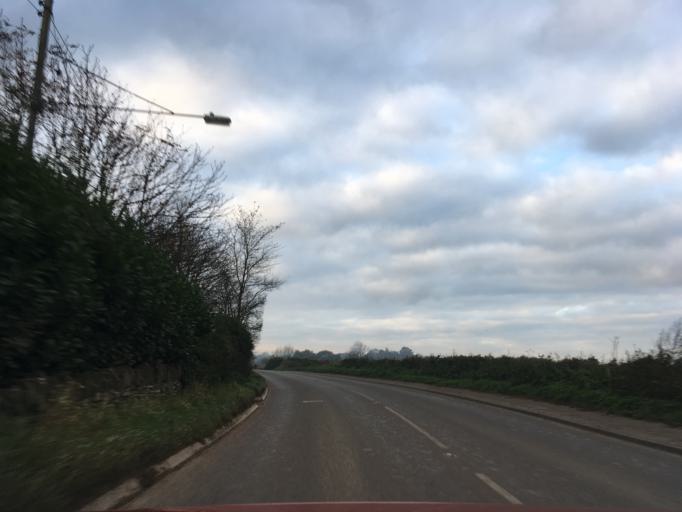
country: GB
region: England
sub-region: South Gloucestershire
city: Yate
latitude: 51.5566
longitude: -2.4543
